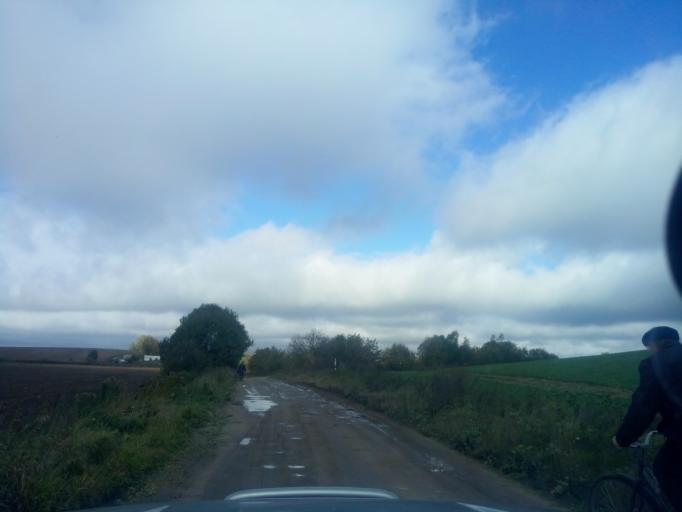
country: BY
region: Minsk
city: Zaslawye
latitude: 54.0206
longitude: 27.2898
